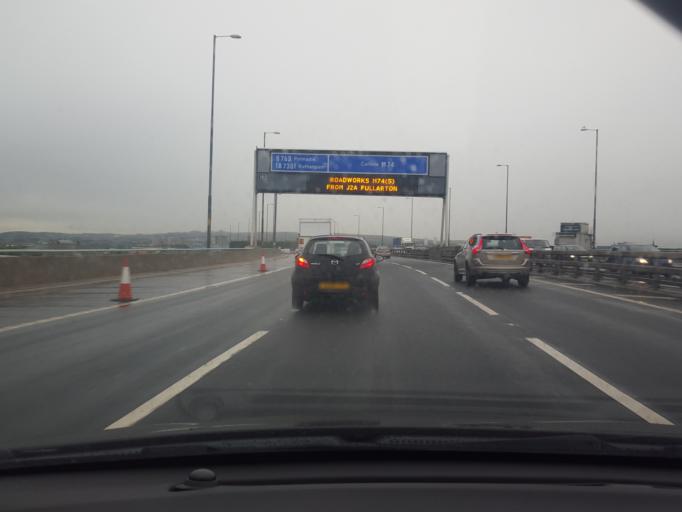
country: GB
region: Scotland
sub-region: Glasgow City
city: Glasgow
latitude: 55.8483
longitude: -4.2633
